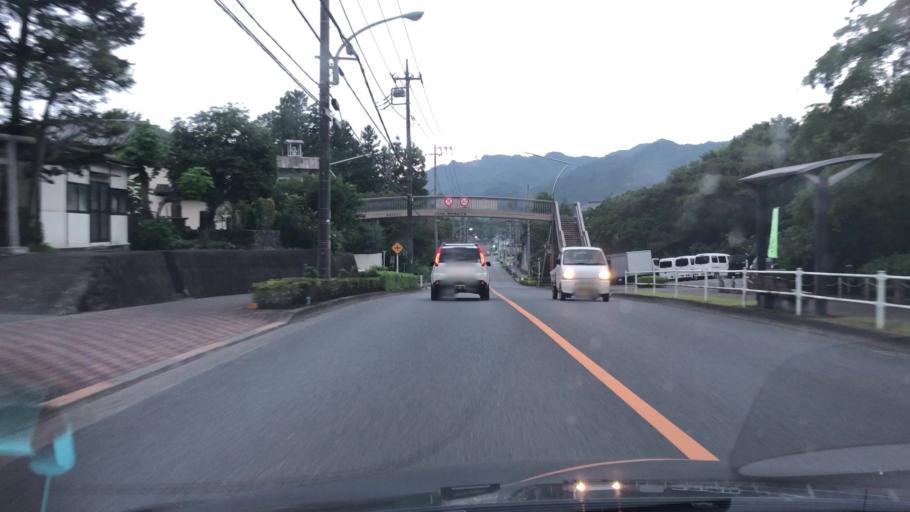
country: JP
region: Tokyo
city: Ome
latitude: 35.7870
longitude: 139.2236
